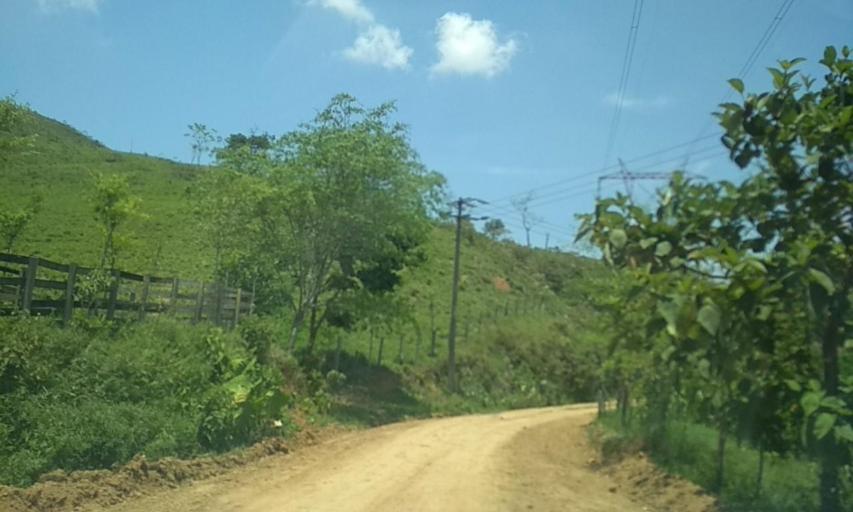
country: MX
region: Chiapas
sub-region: Tecpatan
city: Raudales Malpaso
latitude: 17.3961
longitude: -93.7451
